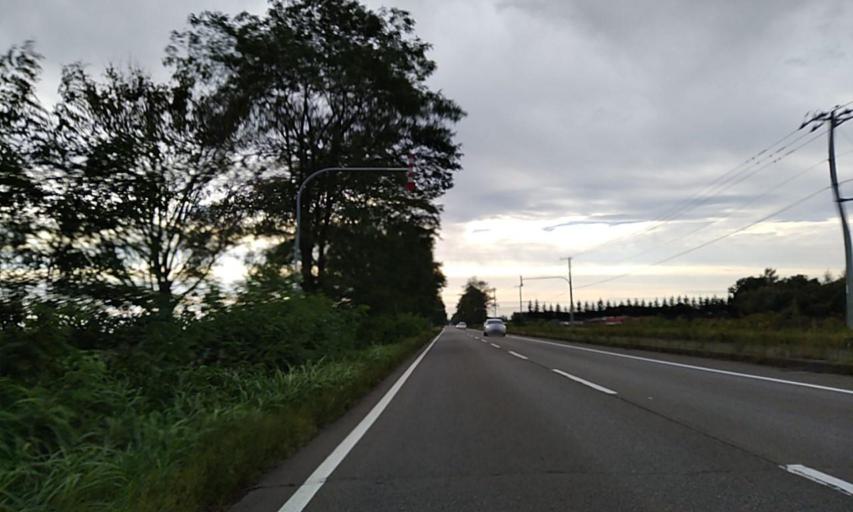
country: JP
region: Hokkaido
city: Obihiro
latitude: 42.9279
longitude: 142.9838
